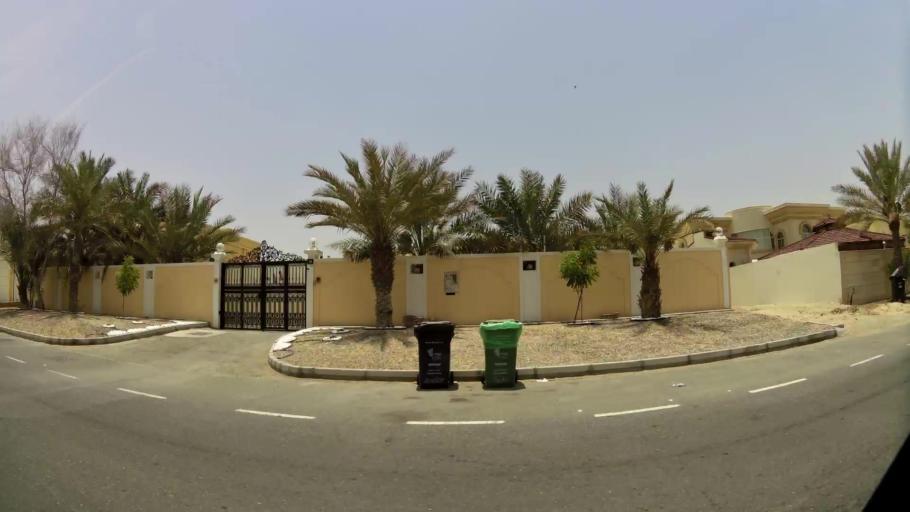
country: AE
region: Ash Shariqah
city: Sharjah
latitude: 25.2101
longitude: 55.3899
